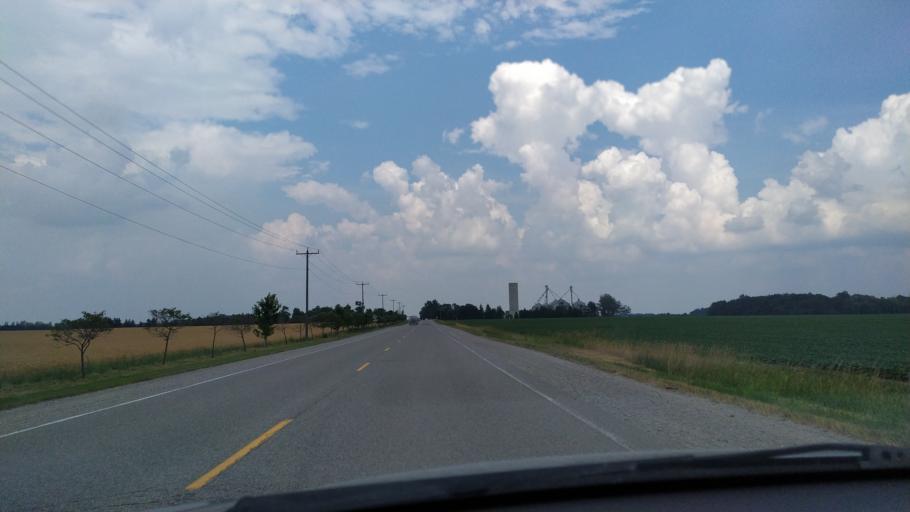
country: CA
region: Ontario
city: London
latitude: 43.1581
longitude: -81.1663
